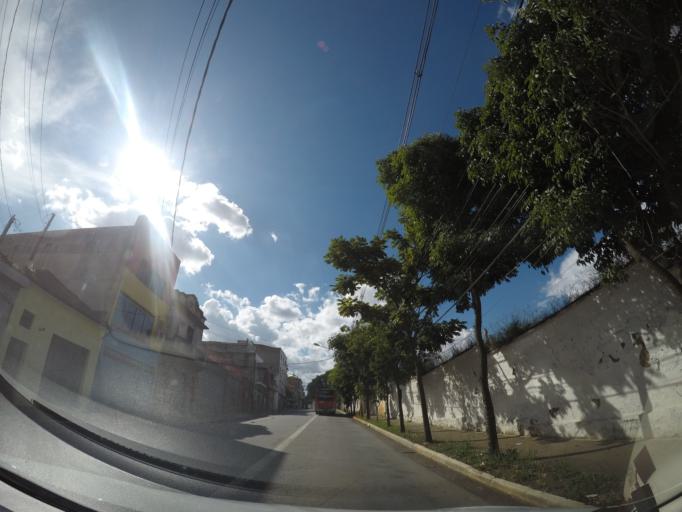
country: BR
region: Sao Paulo
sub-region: Sao Paulo
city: Sao Paulo
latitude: -23.5484
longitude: -46.5820
